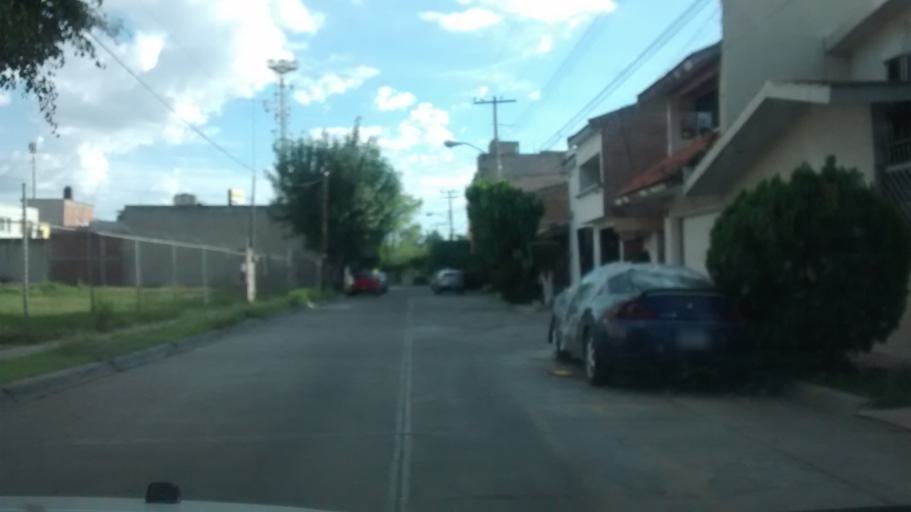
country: MX
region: Guanajuato
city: Leon
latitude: 21.1018
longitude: -101.6472
